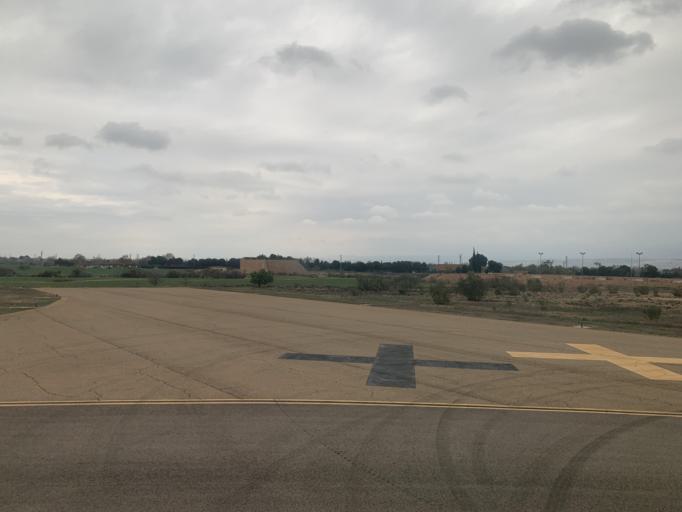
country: ES
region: Aragon
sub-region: Provincia de Zaragoza
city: Utebo
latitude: 41.6710
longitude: -1.0381
